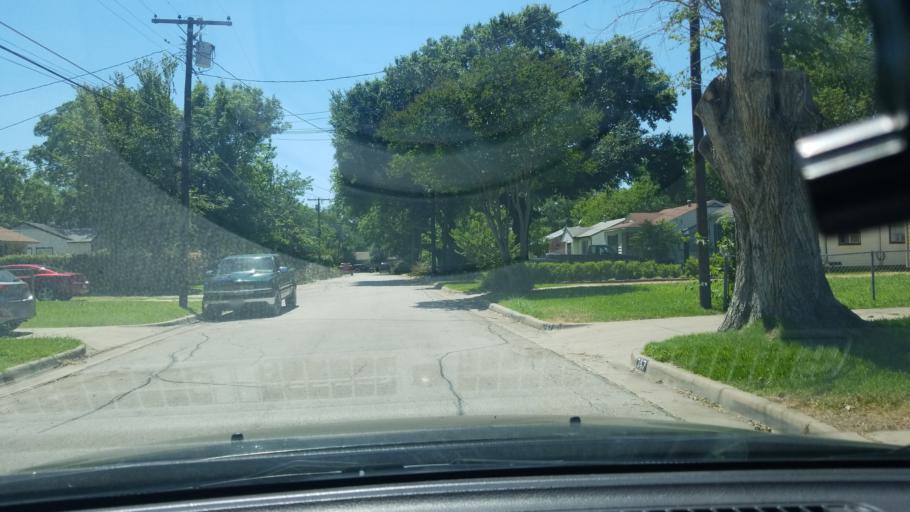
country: US
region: Texas
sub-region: Dallas County
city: Mesquite
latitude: 32.7627
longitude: -96.6078
